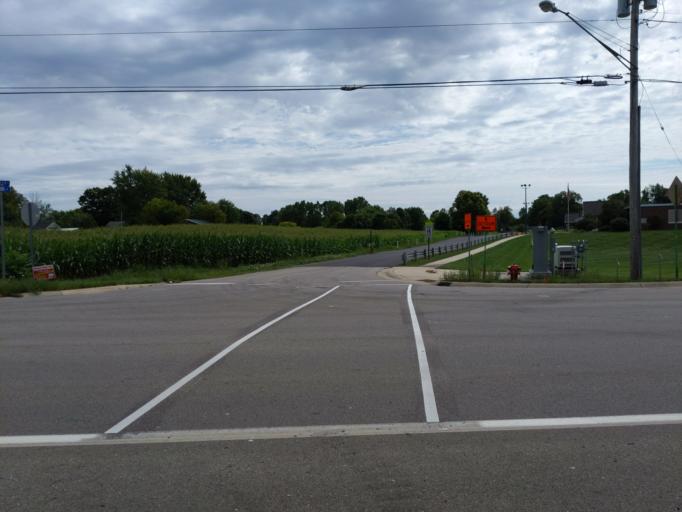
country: US
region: Michigan
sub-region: Barry County
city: Nashville
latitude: 42.5996
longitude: -85.0967
